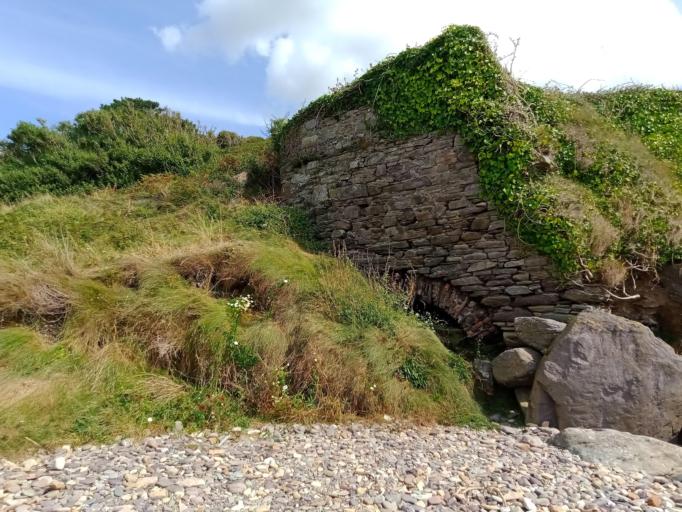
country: IE
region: Munster
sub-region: Waterford
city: Dungarvan
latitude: 52.1064
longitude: -7.5101
